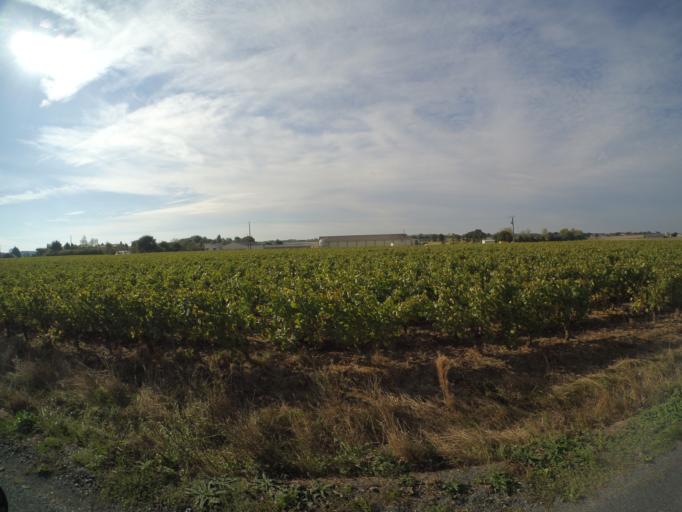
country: FR
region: Pays de la Loire
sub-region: Departement de Maine-et-Loire
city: Tillieres
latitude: 47.1380
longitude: -1.1708
